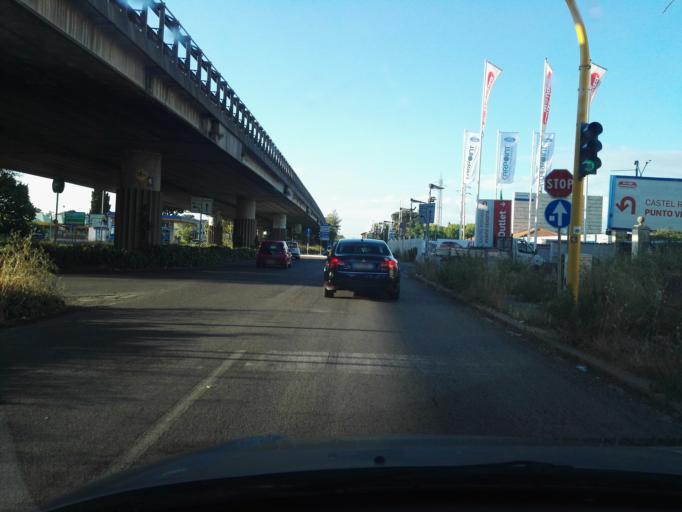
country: IT
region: Latium
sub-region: Citta metropolitana di Roma Capitale
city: Selcetta
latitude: 41.7924
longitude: 12.4520
